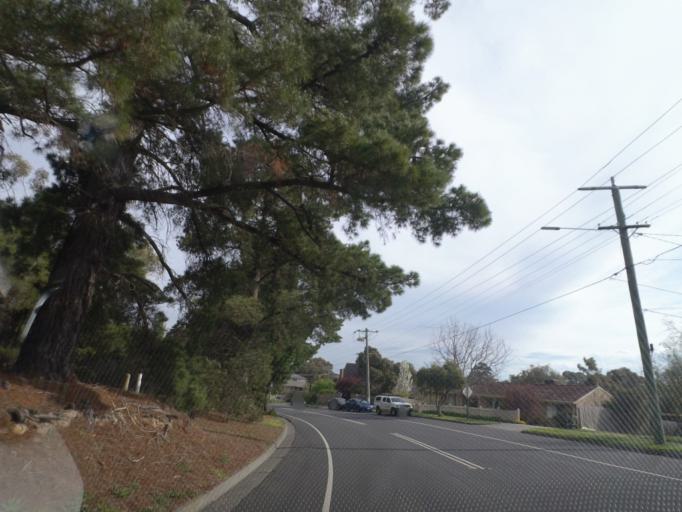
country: AU
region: Victoria
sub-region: Whitehorse
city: Vermont South
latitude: -37.8557
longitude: 145.1988
